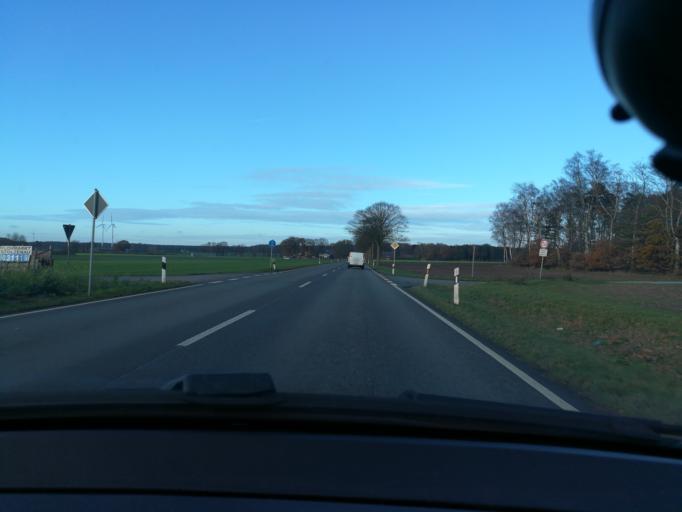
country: DE
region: Lower Saxony
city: Kirchdorf
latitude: 52.5552
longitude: 8.8587
